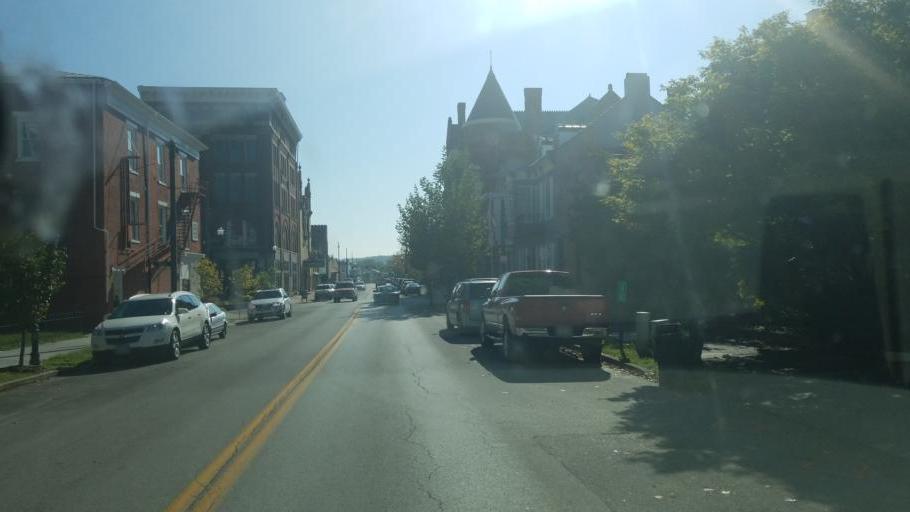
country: US
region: Ohio
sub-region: Brown County
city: Aberdeen
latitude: 38.6471
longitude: -83.7658
